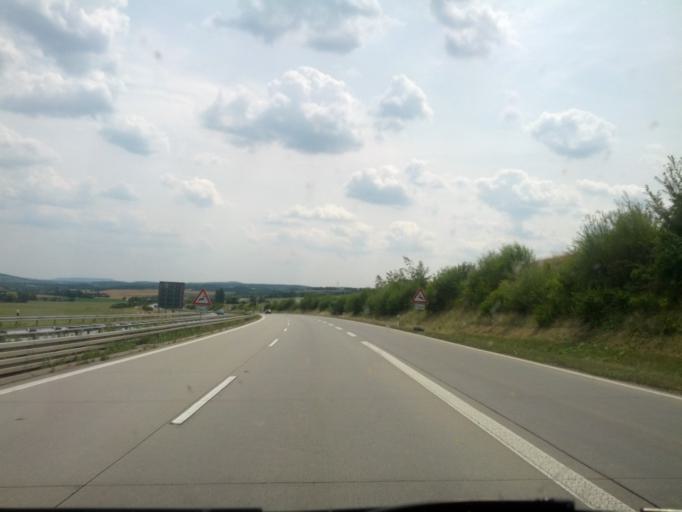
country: DE
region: Saxony
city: Dohna
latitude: 50.9445
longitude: 13.8741
